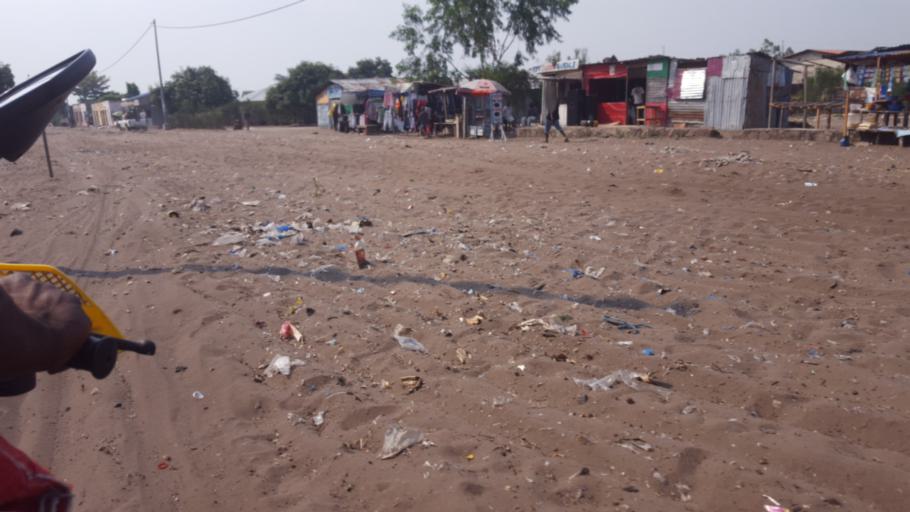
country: CD
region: Kinshasa
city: Masina
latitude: -4.3620
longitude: 15.5091
